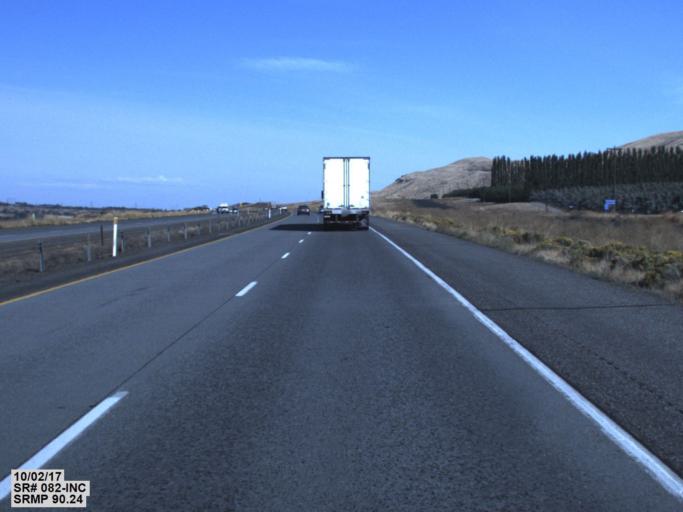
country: US
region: Washington
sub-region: Benton County
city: Benton City
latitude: 46.2544
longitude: -119.6003
